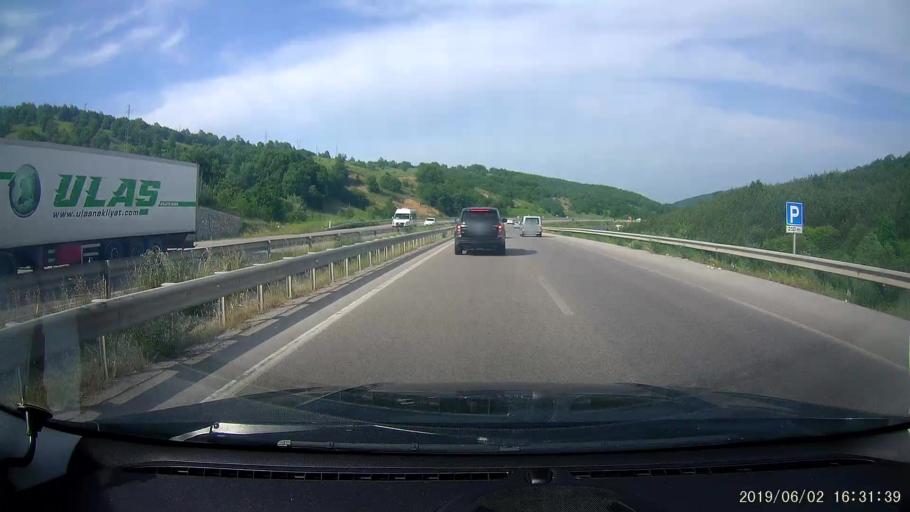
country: TR
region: Samsun
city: Ladik
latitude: 41.0341
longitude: 35.9041
